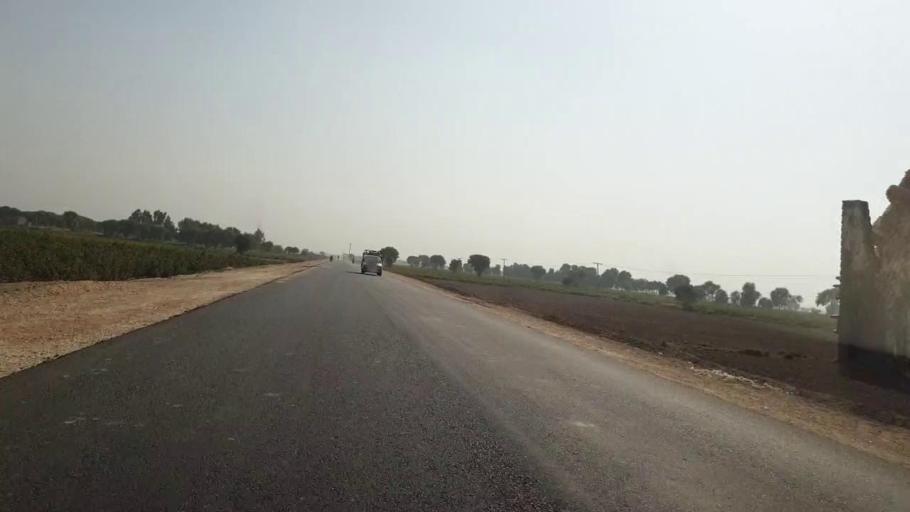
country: PK
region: Sindh
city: Dadu
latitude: 26.6645
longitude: 67.7764
